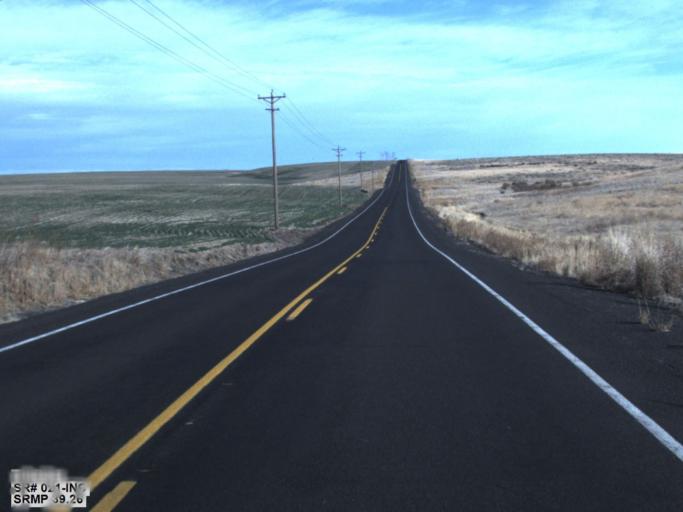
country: US
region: Washington
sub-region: Adams County
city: Ritzville
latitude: 47.1179
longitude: -118.6653
